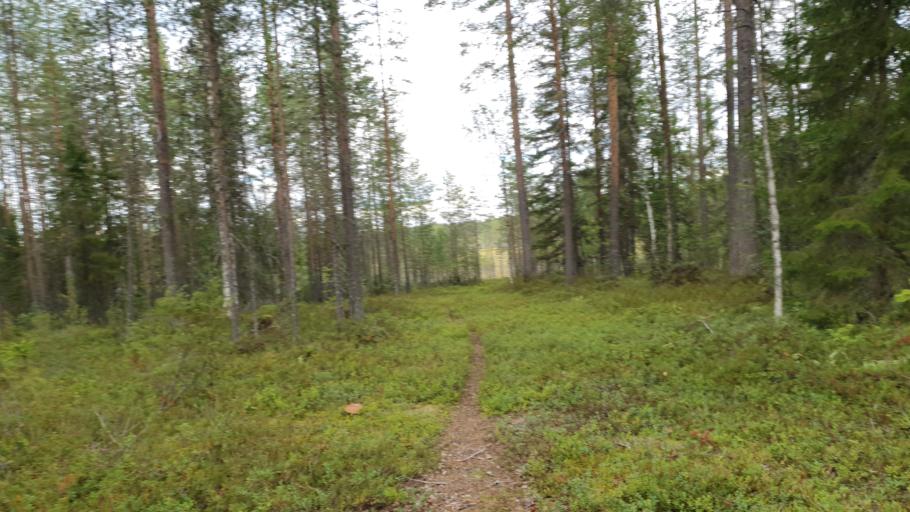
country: FI
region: Kainuu
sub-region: Kehys-Kainuu
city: Kuhmo
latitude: 64.0856
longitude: 29.5275
